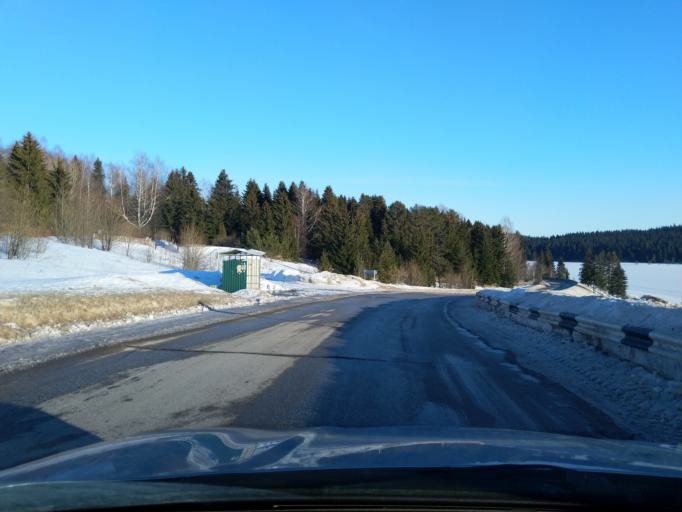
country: RU
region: Perm
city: Polazna
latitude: 58.3056
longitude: 56.4275
